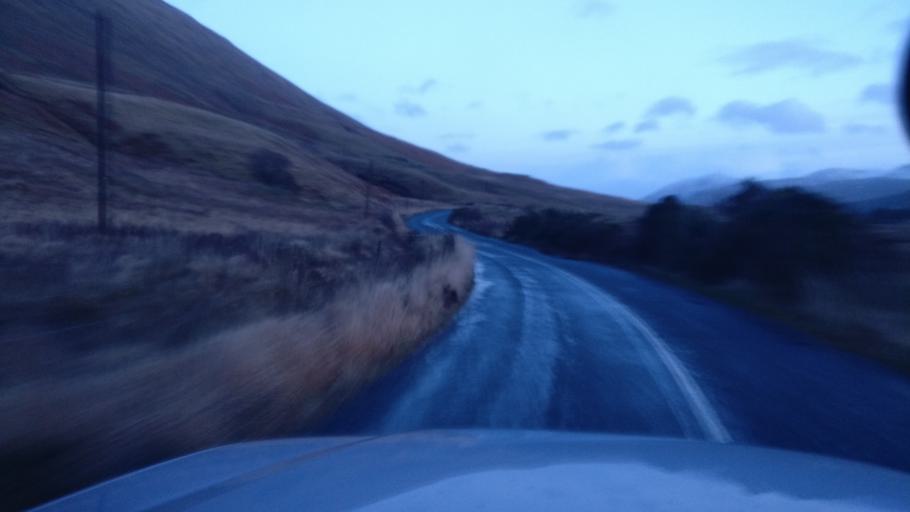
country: IE
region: Connaught
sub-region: Maigh Eo
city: Westport
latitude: 53.5661
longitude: -9.6521
